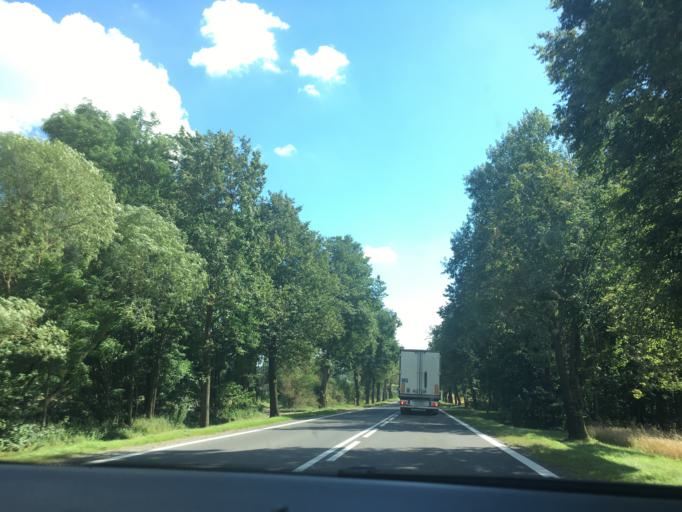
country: PL
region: Podlasie
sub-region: Powiat sokolski
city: Suchowola
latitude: 53.6390
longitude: 23.1199
